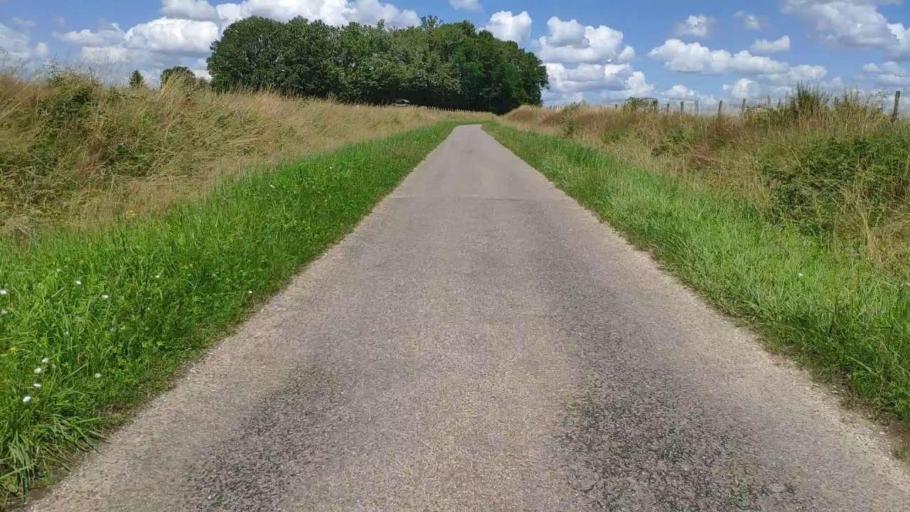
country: FR
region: Franche-Comte
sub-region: Departement du Jura
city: Chaussin
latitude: 46.8749
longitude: 5.4747
